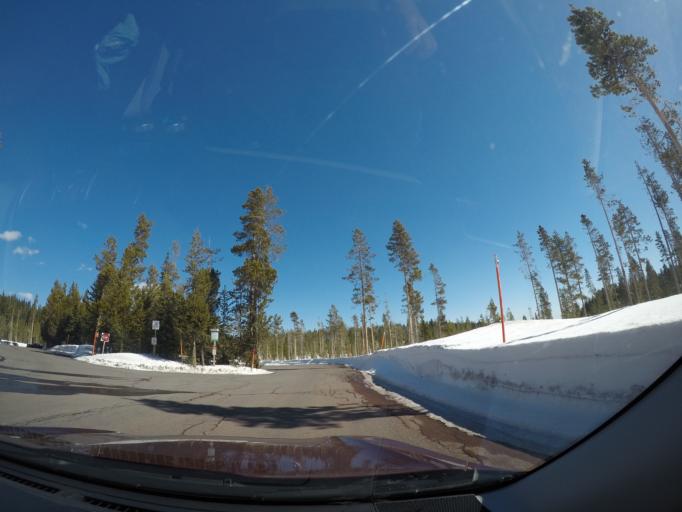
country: US
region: Oregon
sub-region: Deschutes County
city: Sunriver
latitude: 43.9887
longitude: -121.5685
